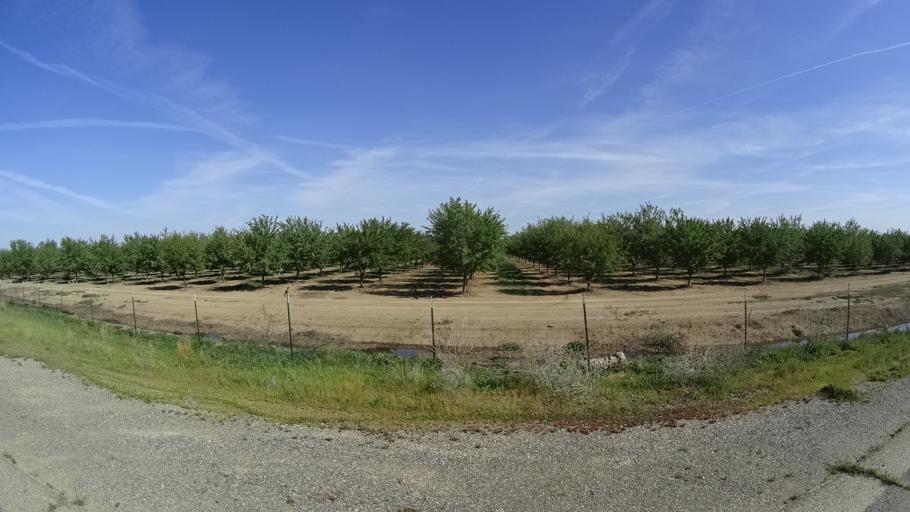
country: US
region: California
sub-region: Glenn County
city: Willows
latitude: 39.6114
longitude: -122.2049
